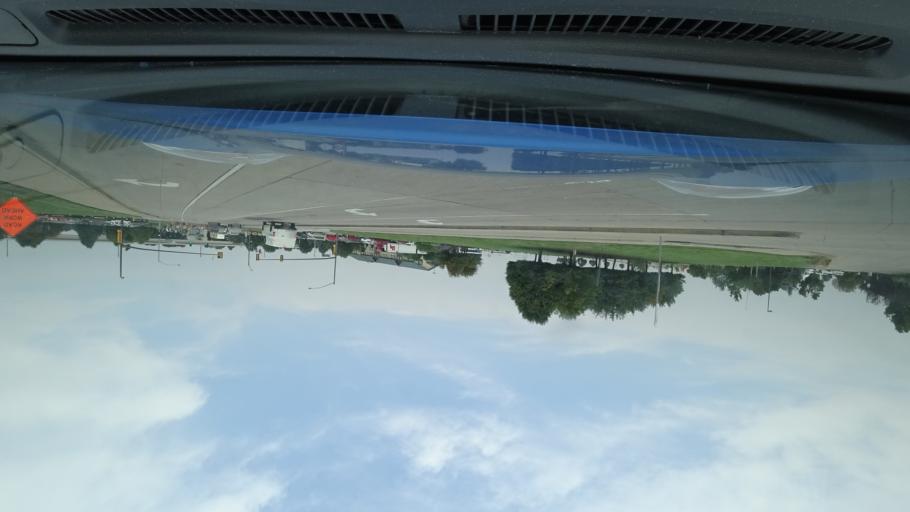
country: US
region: Colorado
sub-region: Adams County
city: Aurora
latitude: 39.7618
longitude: -104.7924
